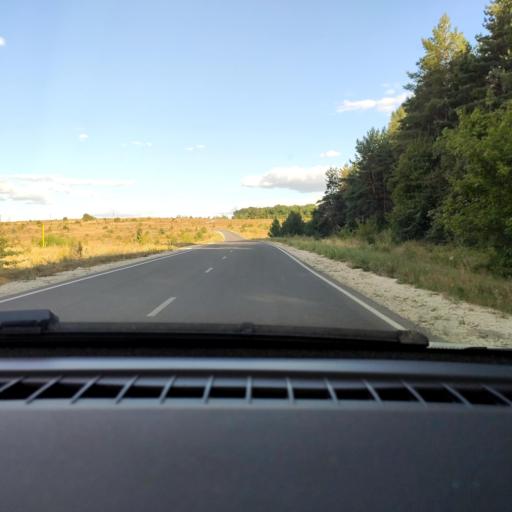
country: RU
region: Voronezj
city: Semiluki
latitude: 51.6573
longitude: 38.9948
